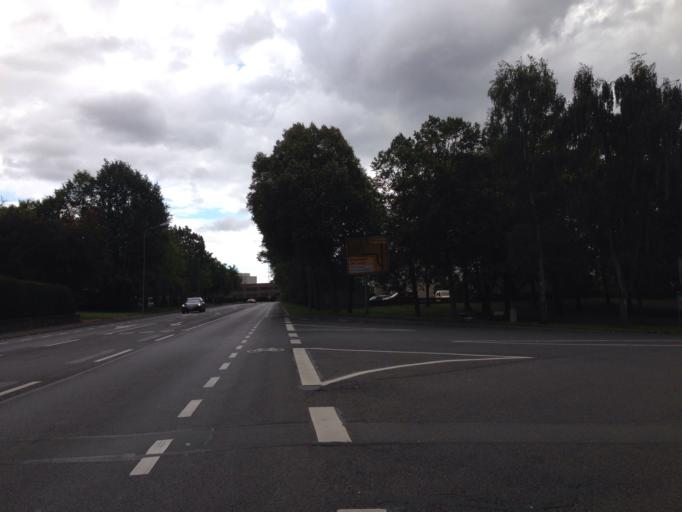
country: DE
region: Hesse
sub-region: Regierungsbezirk Giessen
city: Limburg an der Lahn
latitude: 50.3743
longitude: 8.0634
